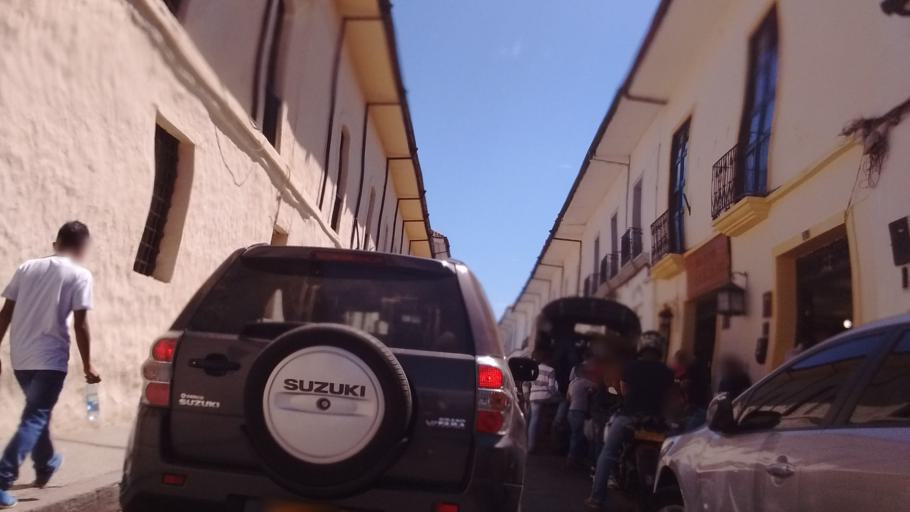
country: CO
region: Cauca
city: Popayan
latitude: 2.4403
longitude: -76.6053
